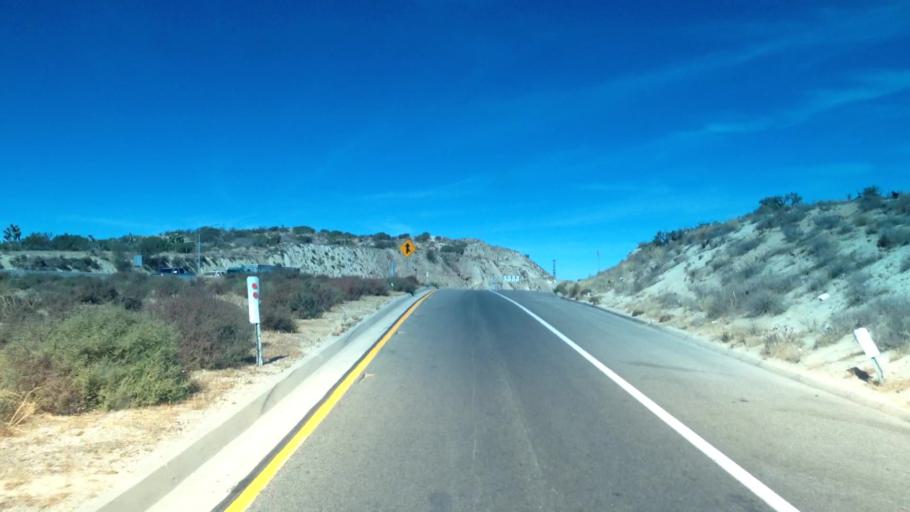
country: US
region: California
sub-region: Los Angeles County
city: Palmdale
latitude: 34.5591
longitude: -118.1321
